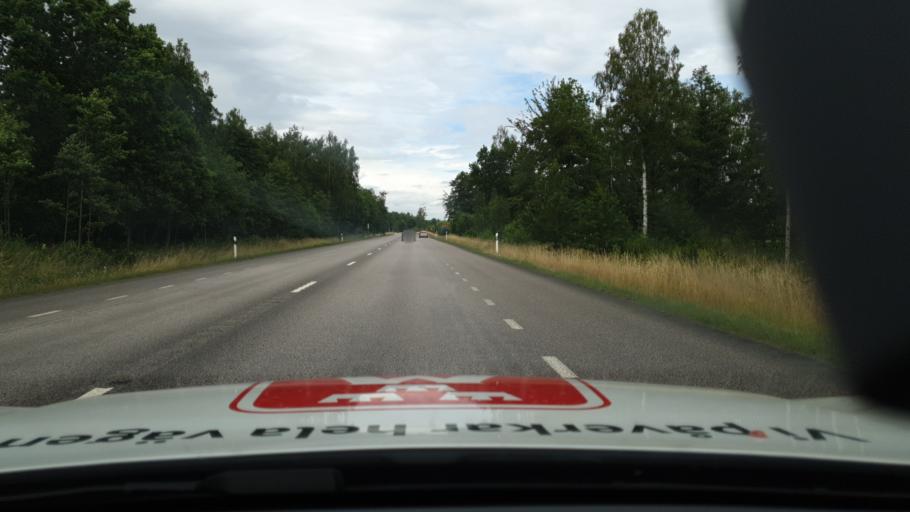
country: SE
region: Vaestra Goetaland
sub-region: Hjo Kommun
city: Hjo
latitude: 58.2870
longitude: 14.2615
